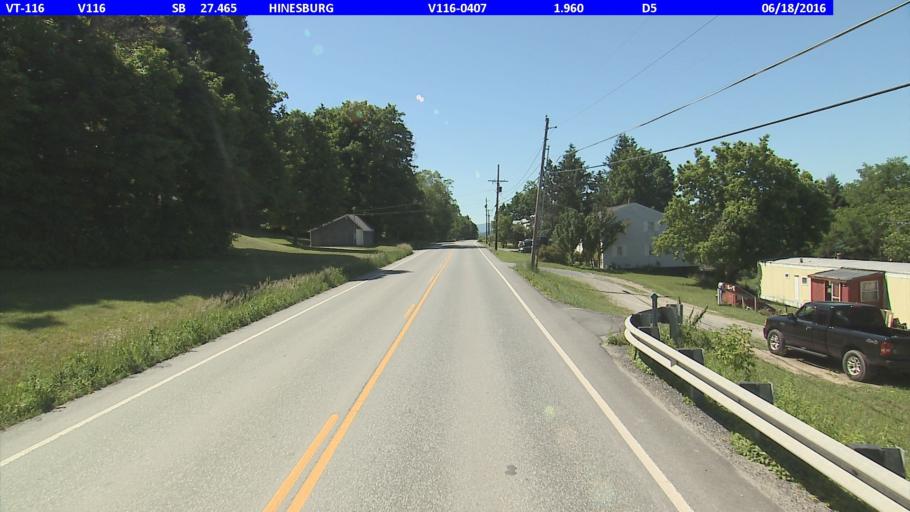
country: US
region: Vermont
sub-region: Chittenden County
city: Hinesburg
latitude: 44.3078
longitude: -73.0750
